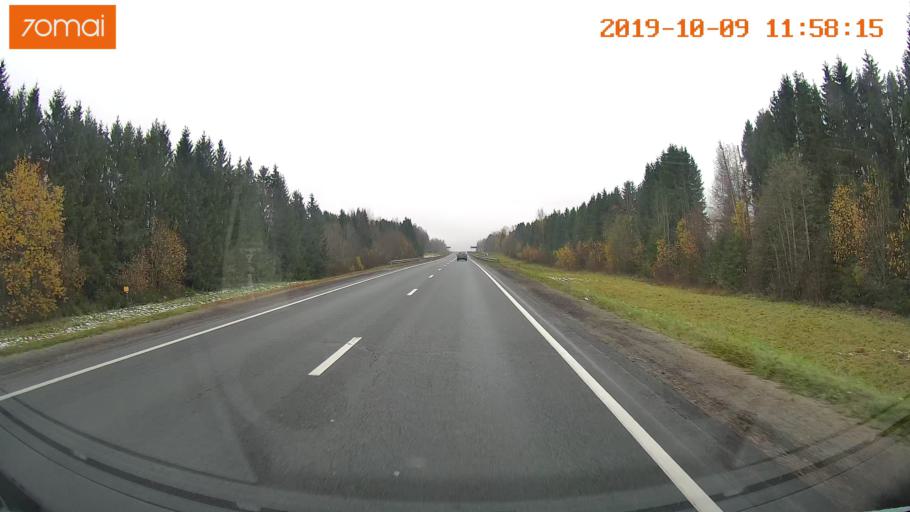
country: RU
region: Vologda
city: Gryazovets
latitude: 58.7206
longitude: 40.2962
